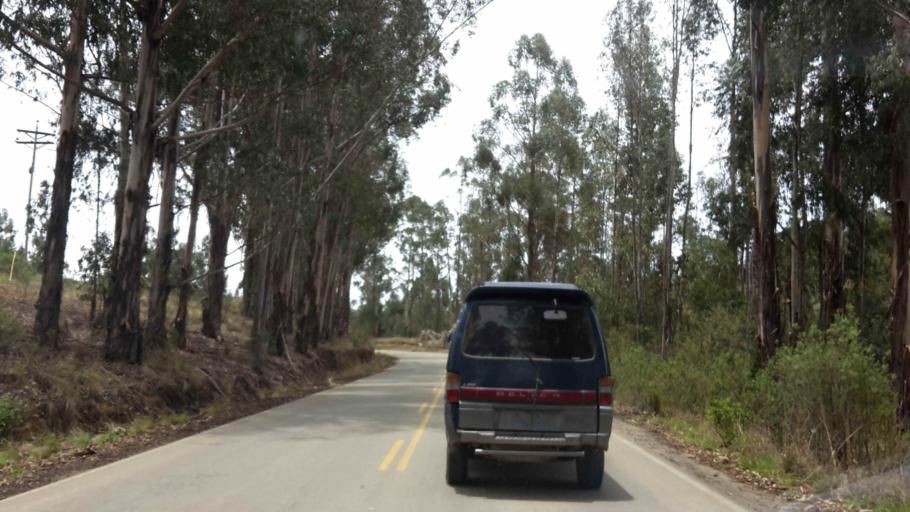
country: BO
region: Cochabamba
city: Totora
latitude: -17.7170
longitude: -65.2051
